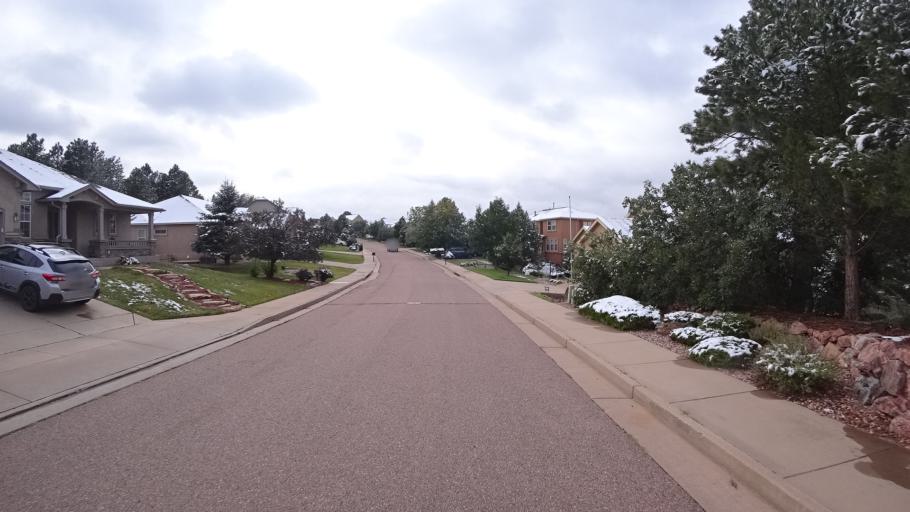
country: US
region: Colorado
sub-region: El Paso County
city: Colorado Springs
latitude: 38.9142
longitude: -104.7953
